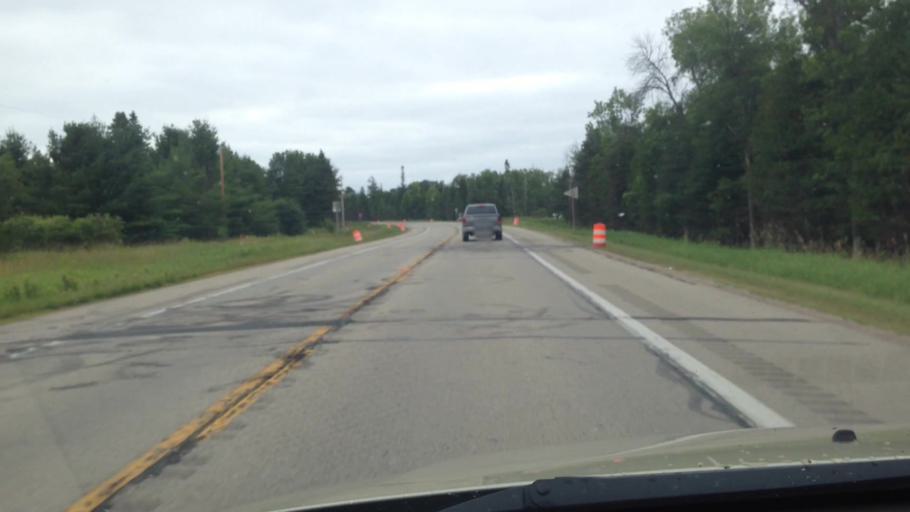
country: US
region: Michigan
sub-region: Delta County
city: Escanaba
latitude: 45.5959
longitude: -87.2309
